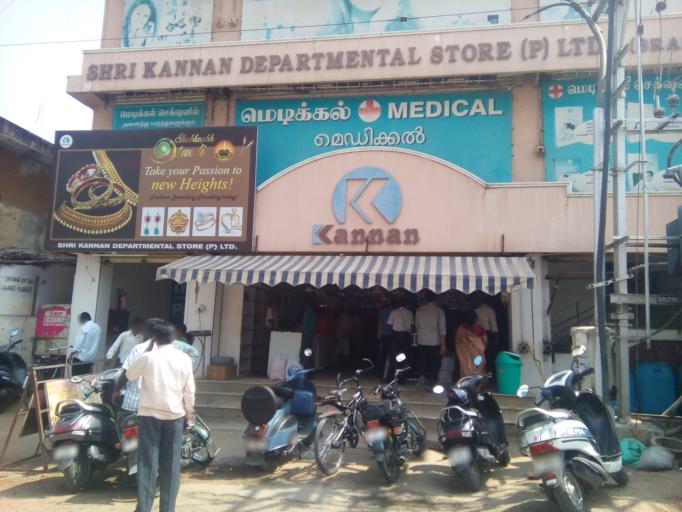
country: IN
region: Tamil Nadu
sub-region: Coimbatore
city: Coimbatore
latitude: 11.0166
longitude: 76.9632
